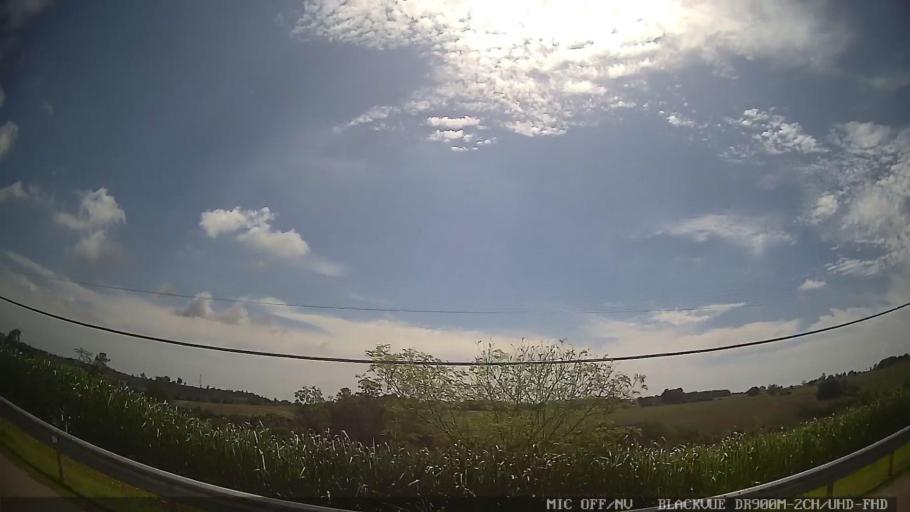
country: BR
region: Sao Paulo
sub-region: Tiete
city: Tiete
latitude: -23.1241
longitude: -47.6990
